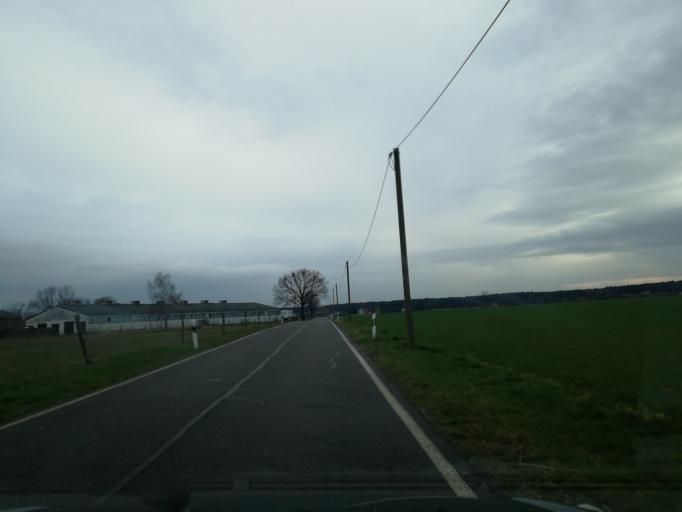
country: DE
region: Brandenburg
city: Calau
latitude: 51.7368
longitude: 14.0210
